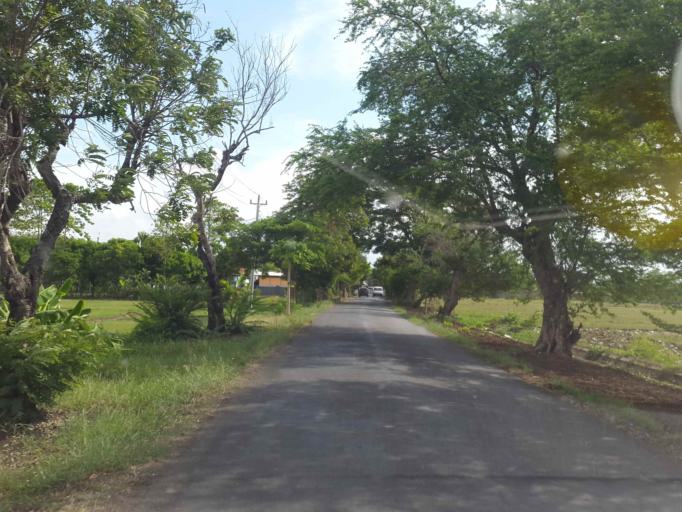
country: ID
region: Central Java
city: Pemalang
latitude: -6.8911
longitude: 109.3275
